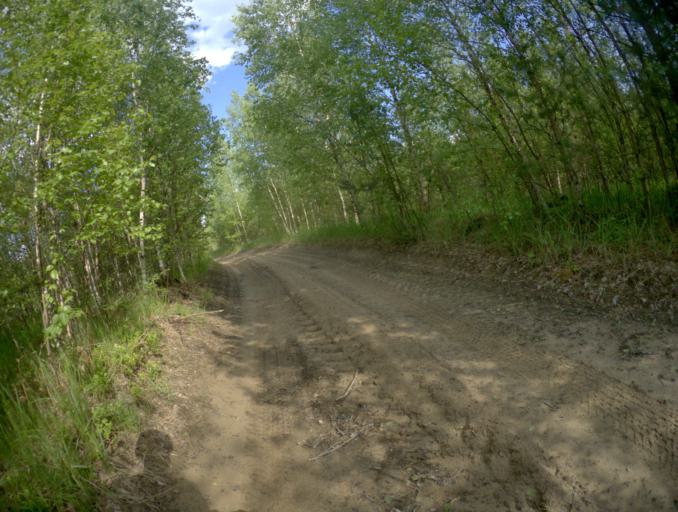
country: RU
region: Vladimir
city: Zolotkovo
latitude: 55.3301
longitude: 40.9769
